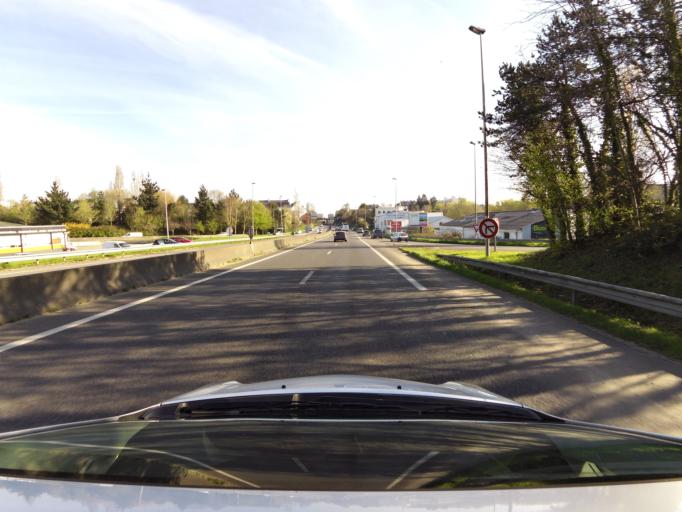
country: FR
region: Brittany
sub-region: Departement du Morbihan
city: Lorient
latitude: 47.7575
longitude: -3.3852
